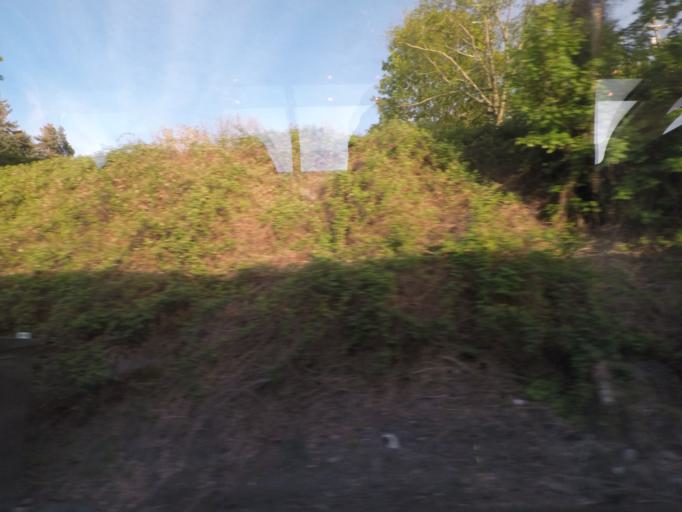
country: US
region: Washington
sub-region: Whatcom County
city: Bellingham
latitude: 48.7326
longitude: -122.5004
